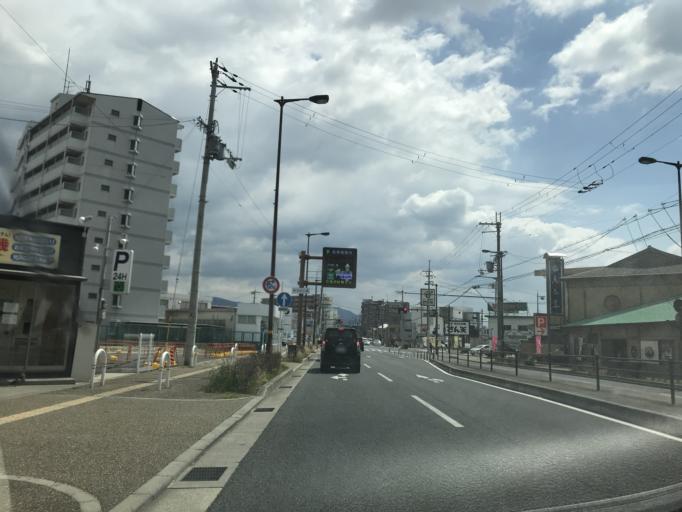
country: JP
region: Nara
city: Nara-shi
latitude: 34.6803
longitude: 135.8112
